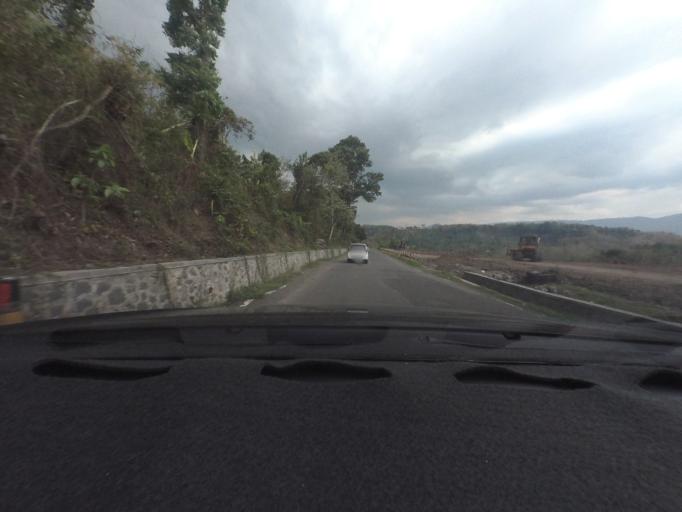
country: ID
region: West Java
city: Sindangsari
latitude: -6.9934
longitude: 106.6665
